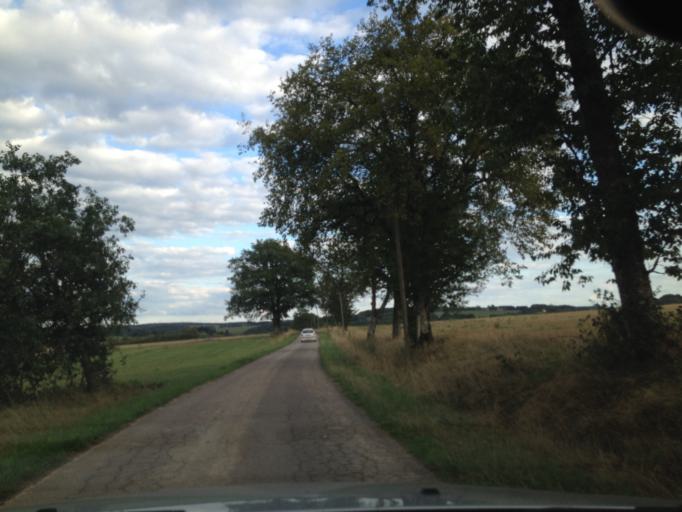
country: FR
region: Lorraine
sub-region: Departement des Vosges
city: Bains-les-Bains
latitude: 47.9862
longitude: 6.1920
